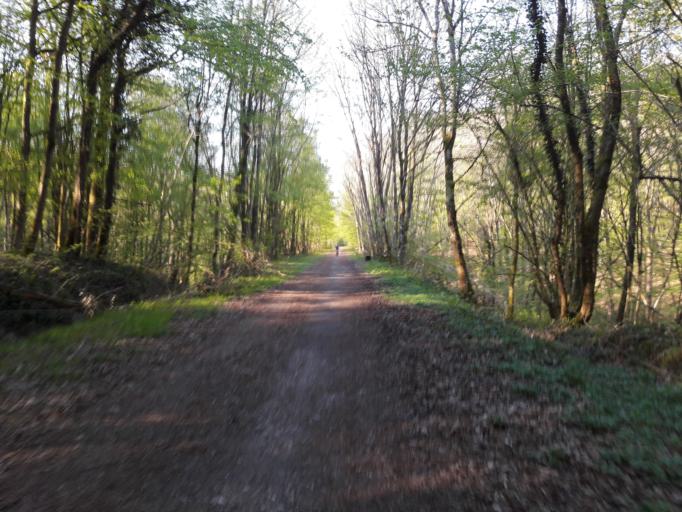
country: FR
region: Nord-Pas-de-Calais
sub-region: Departement du Nord
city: Sains-du-Nord
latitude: 50.1337
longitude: 4.0664
